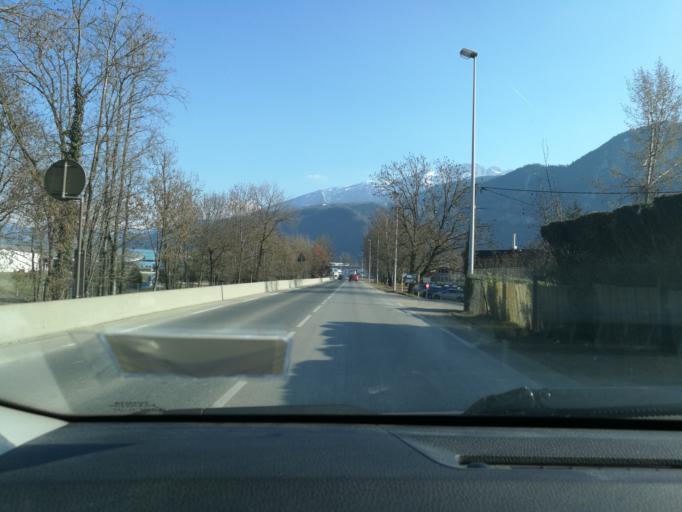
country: FR
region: Rhone-Alpes
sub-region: Departement de la Haute-Savoie
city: Ayse
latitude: 46.0784
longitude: 6.4220
